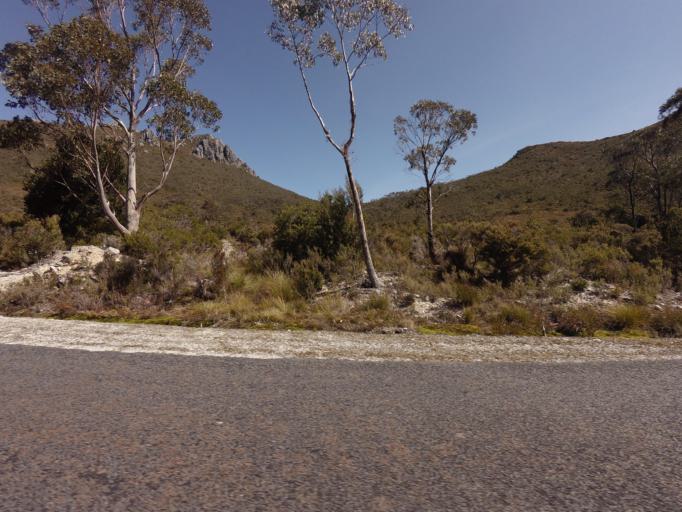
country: AU
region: Tasmania
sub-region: Derwent Valley
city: New Norfolk
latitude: -42.7247
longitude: 146.4498
